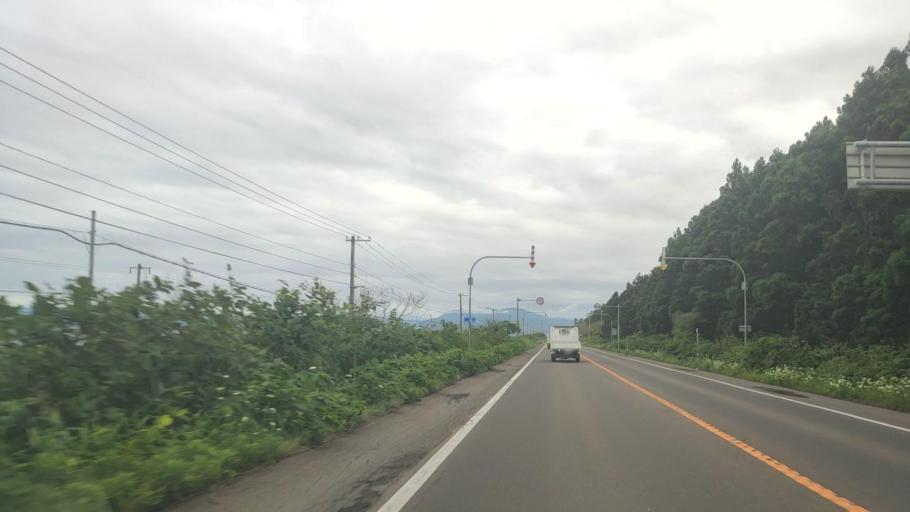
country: JP
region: Hokkaido
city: Niseko Town
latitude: 42.3396
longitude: 140.2804
